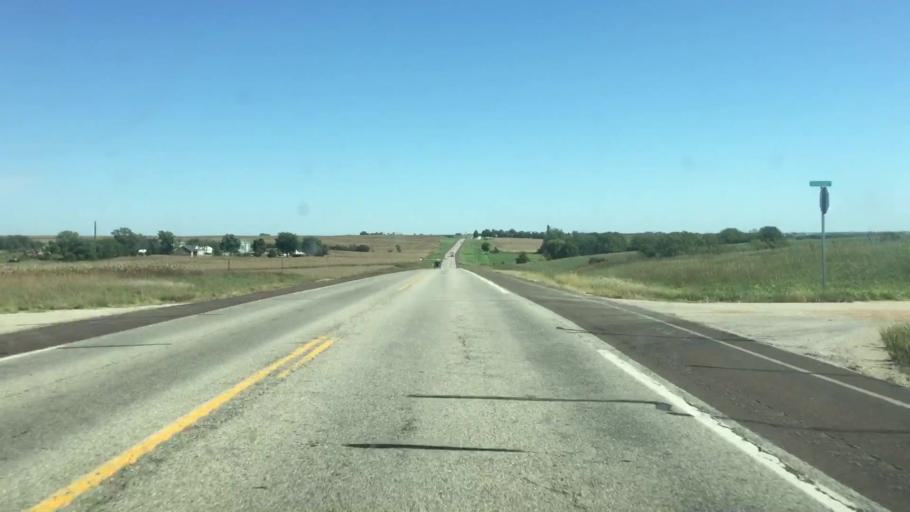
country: US
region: Kansas
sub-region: Nemaha County
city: Seneca
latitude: 39.8421
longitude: -96.3148
